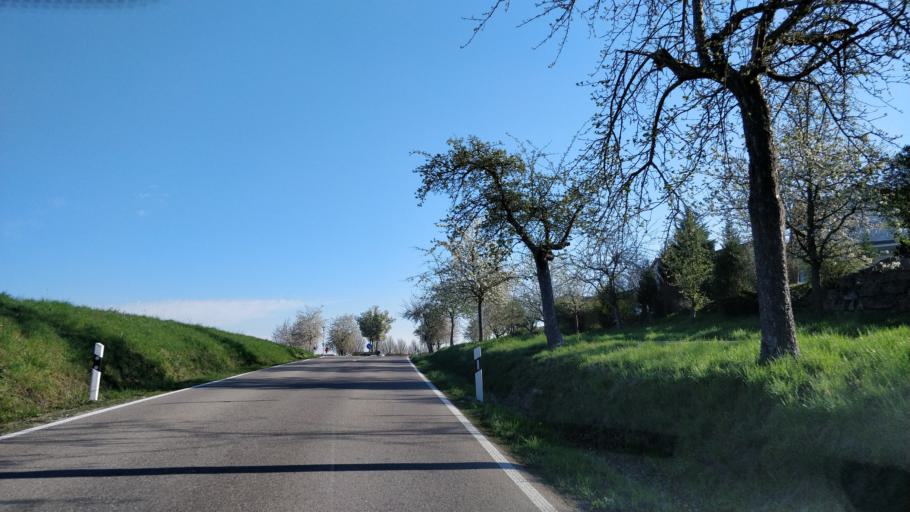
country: DE
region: Baden-Wuerttemberg
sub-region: Regierungsbezirk Stuttgart
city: Michelbach an der Bilz
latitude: 49.0595
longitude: 9.7239
